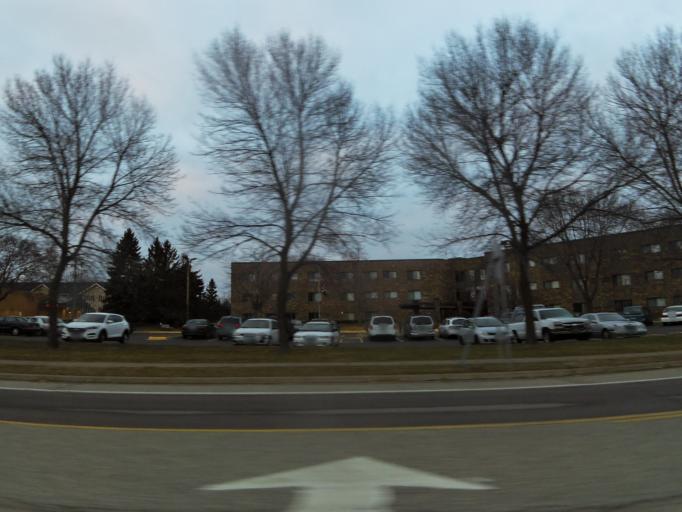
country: US
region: Minnesota
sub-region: Washington County
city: Birchwood
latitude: 45.0502
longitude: -92.9818
